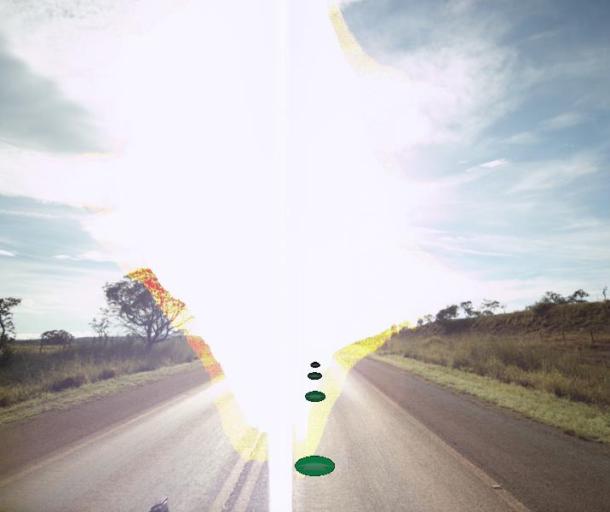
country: BR
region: Goias
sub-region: Pirenopolis
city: Pirenopolis
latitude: -15.7770
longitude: -48.5234
